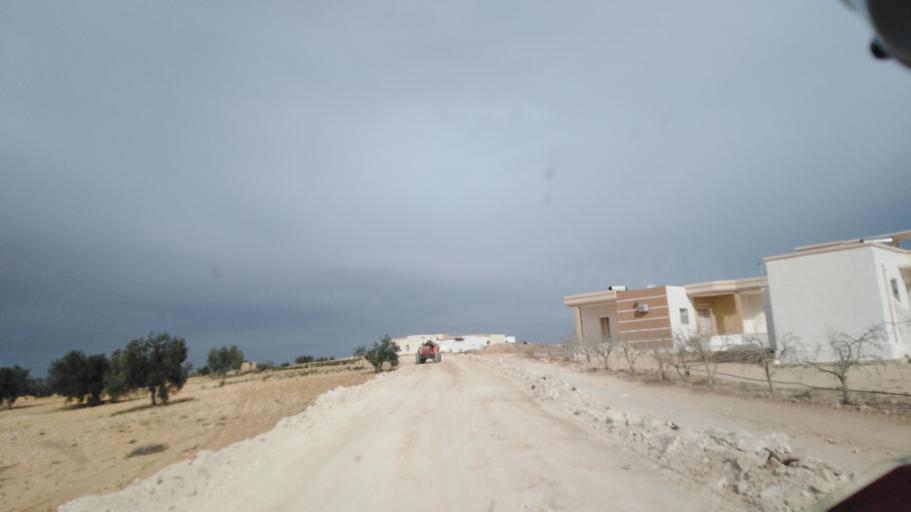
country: TN
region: Safaqis
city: Bi'r `Ali Bin Khalifah
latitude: 34.8139
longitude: 10.3075
